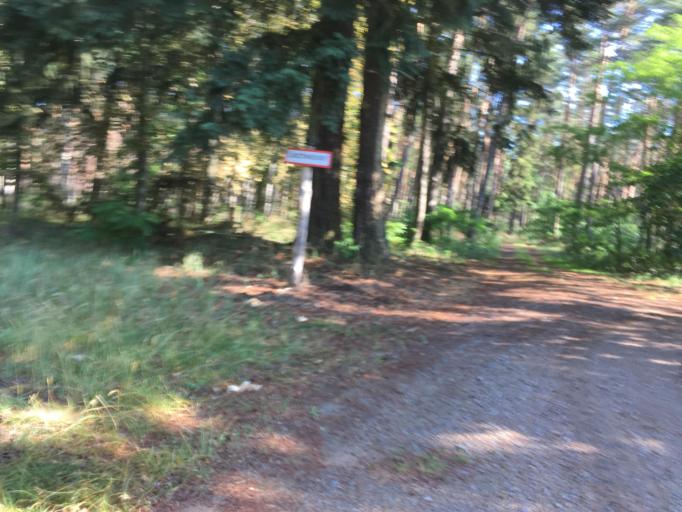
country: DE
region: Brandenburg
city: Marienwerder
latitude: 52.9382
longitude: 13.6055
